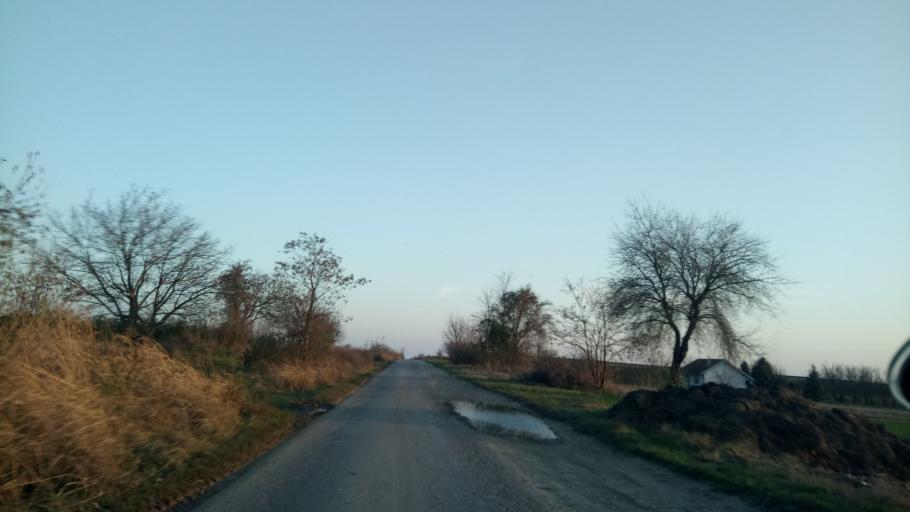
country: RS
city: Novi Slankamen
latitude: 45.1187
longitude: 20.2689
